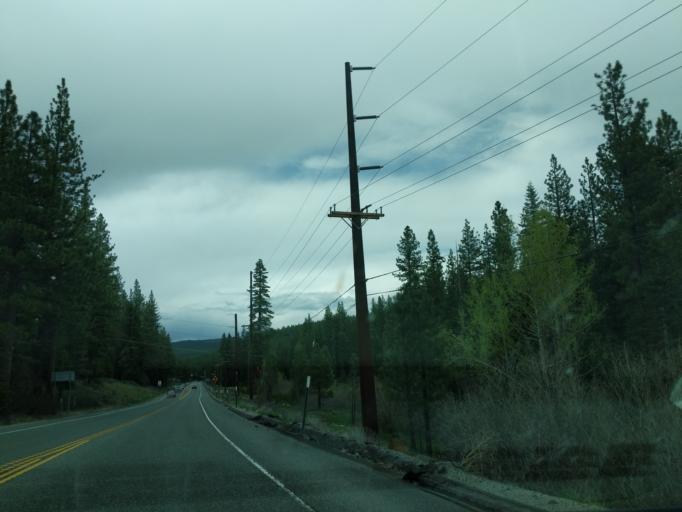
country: US
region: California
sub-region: Placer County
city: Tahoe Vista
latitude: 39.2832
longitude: -120.1046
